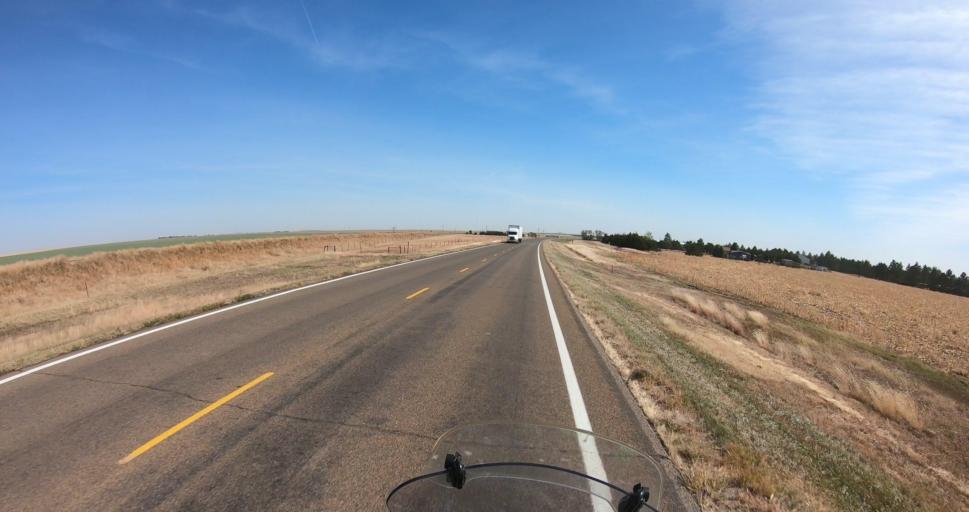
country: US
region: Kansas
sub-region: Thomas County
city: Colby
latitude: 39.3948
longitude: -101.1372
